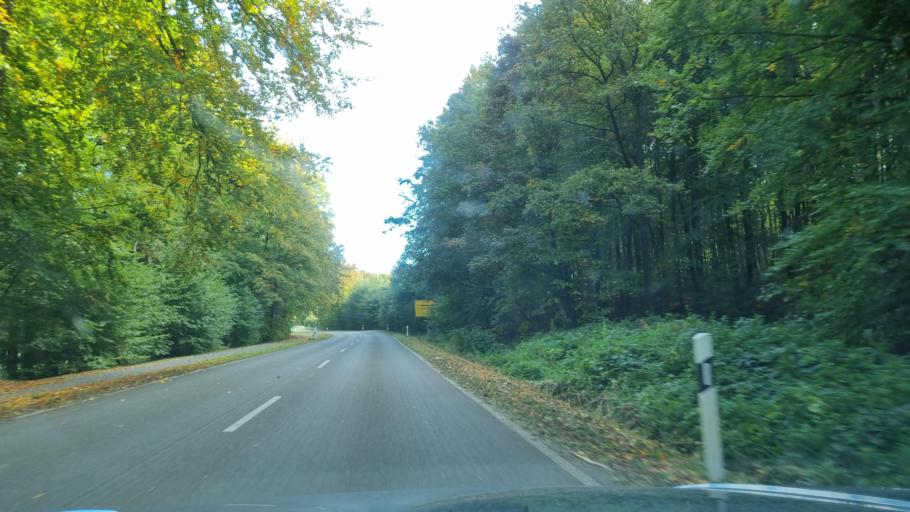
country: DE
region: North Rhine-Westphalia
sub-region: Regierungsbezirk Dusseldorf
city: Kranenburg
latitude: 51.7568
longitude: 6.0340
